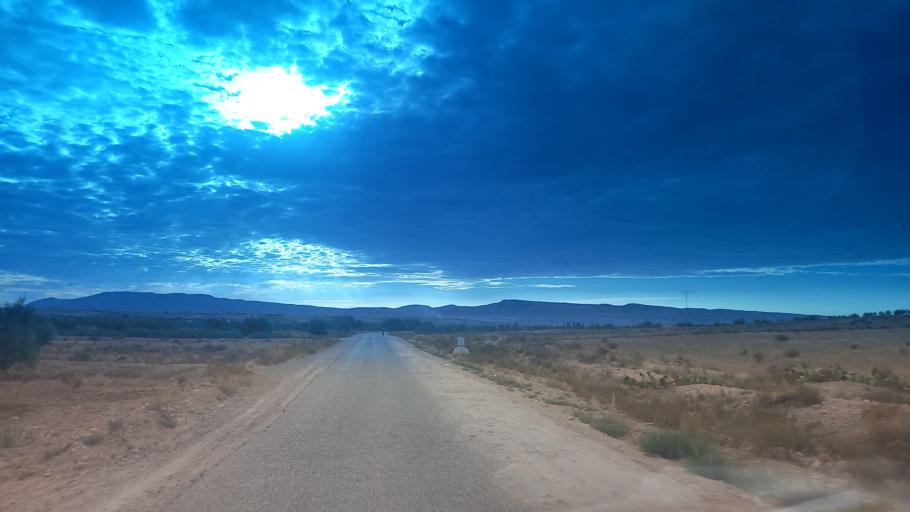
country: TN
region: Al Qasrayn
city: Sbiba
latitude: 35.3831
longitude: 9.0445
